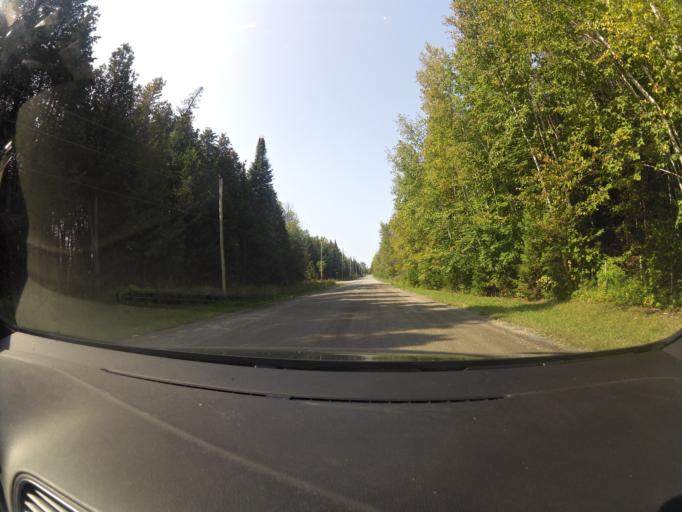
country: CA
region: Ontario
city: Carleton Place
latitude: 45.3273
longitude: -76.1533
